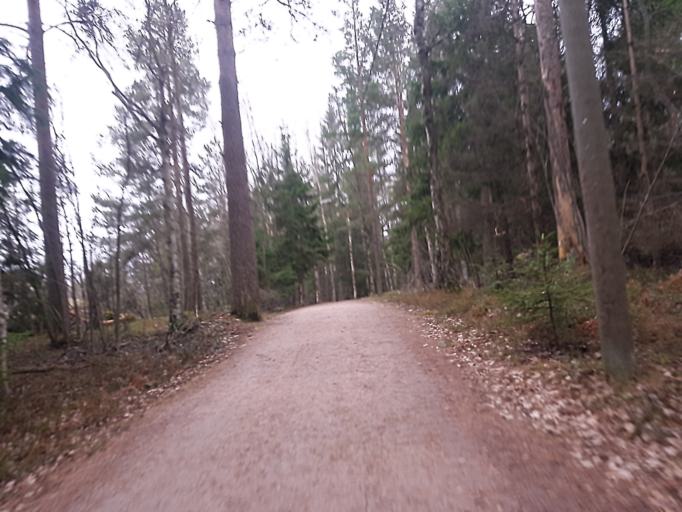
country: FI
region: Uusimaa
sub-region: Helsinki
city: Helsinki
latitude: 60.2193
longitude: 24.9225
